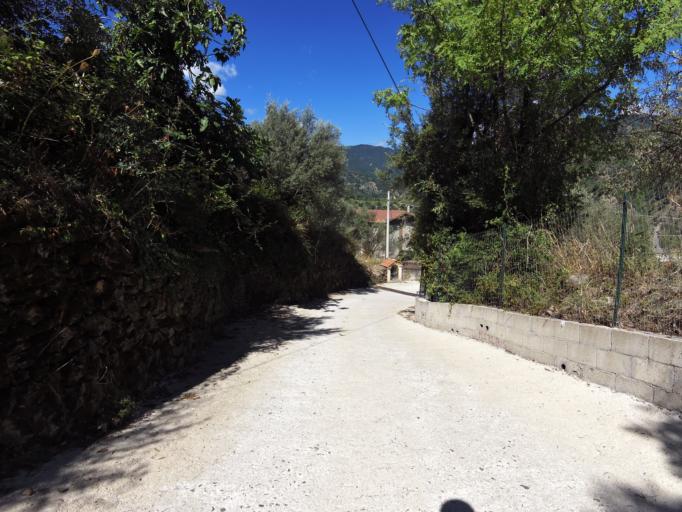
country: IT
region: Calabria
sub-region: Provincia di Reggio Calabria
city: Pazzano
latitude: 38.4797
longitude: 16.4513
